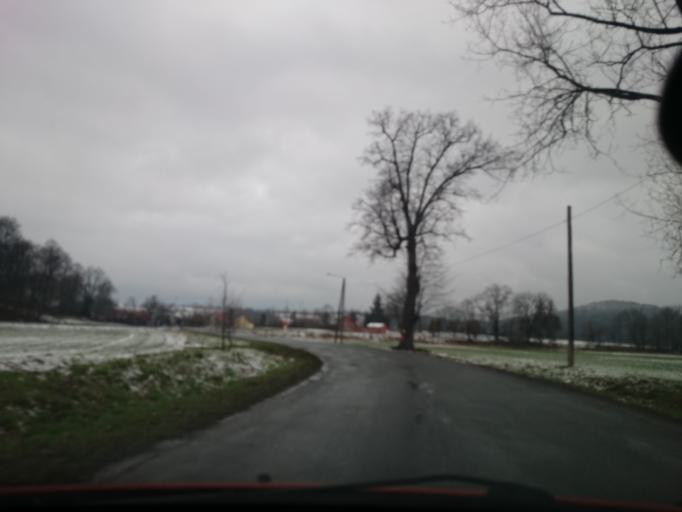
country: PL
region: Lower Silesian Voivodeship
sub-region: Powiat klodzki
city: Klodzko
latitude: 50.3911
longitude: 16.6393
